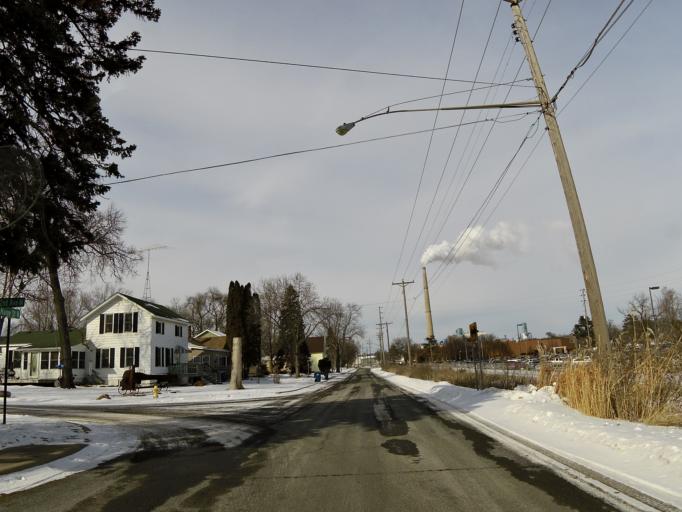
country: US
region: Minnesota
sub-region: Washington County
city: Bayport
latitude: 45.0189
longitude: -92.7770
